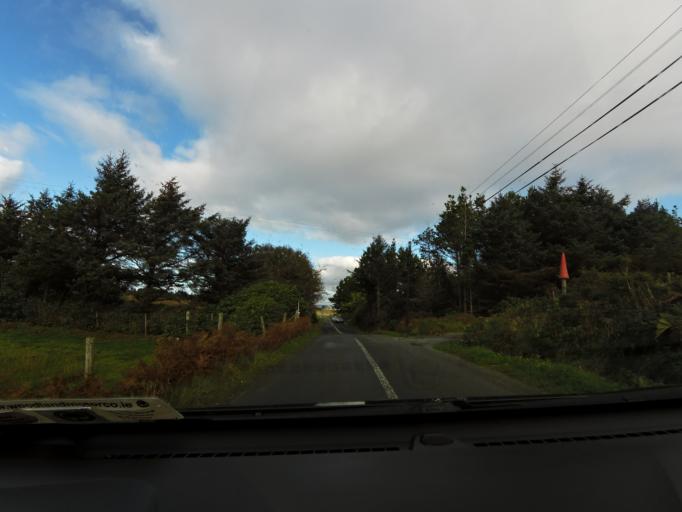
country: IE
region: Connaught
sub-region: Maigh Eo
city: Belmullet
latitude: 53.9389
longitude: -9.8887
